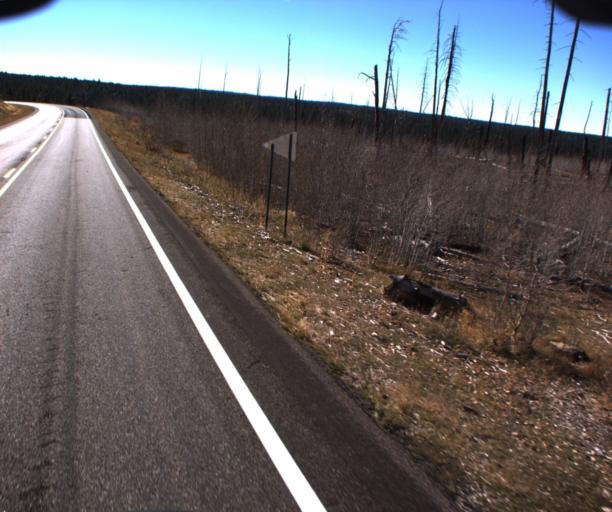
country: US
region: Arizona
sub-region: Coconino County
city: Grand Canyon
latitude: 36.5486
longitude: -112.1805
